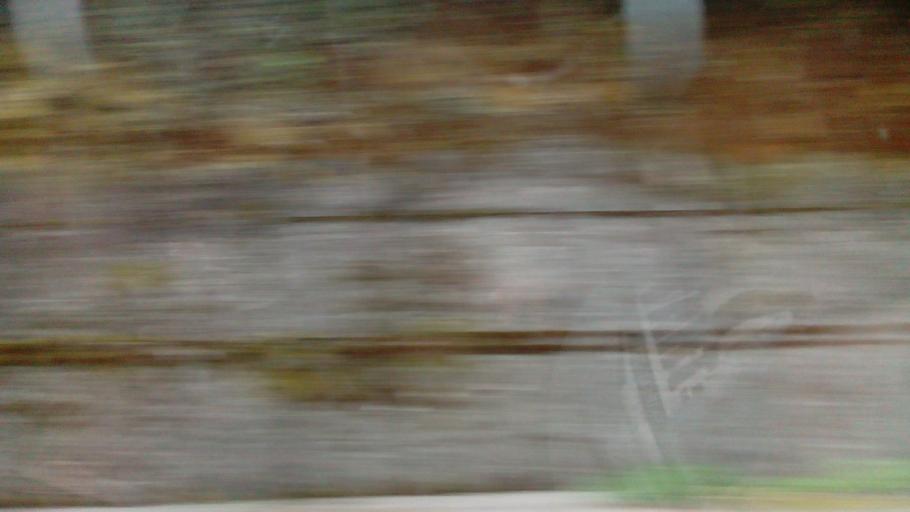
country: TW
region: Taiwan
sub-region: Hualien
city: Hualian
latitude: 24.3630
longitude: 121.3346
